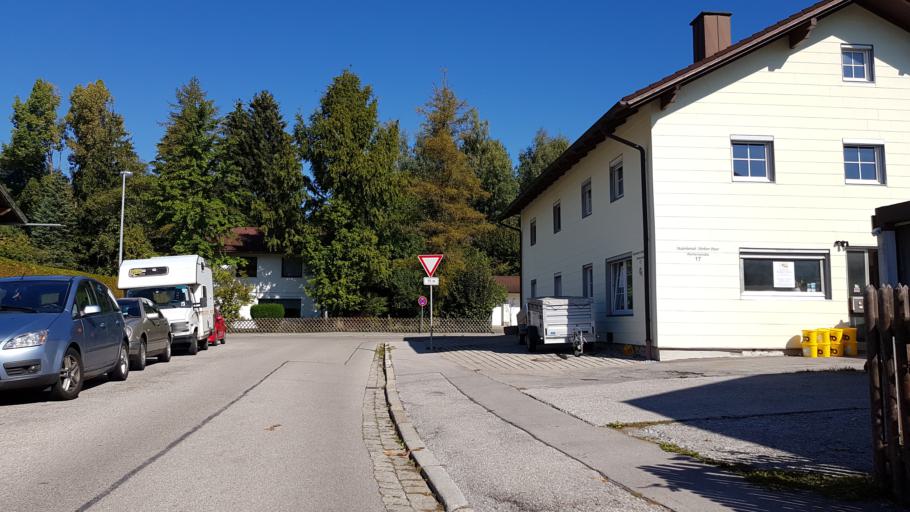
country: DE
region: Bavaria
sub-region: Swabia
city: Fuessen
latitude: 47.5725
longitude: 10.6819
